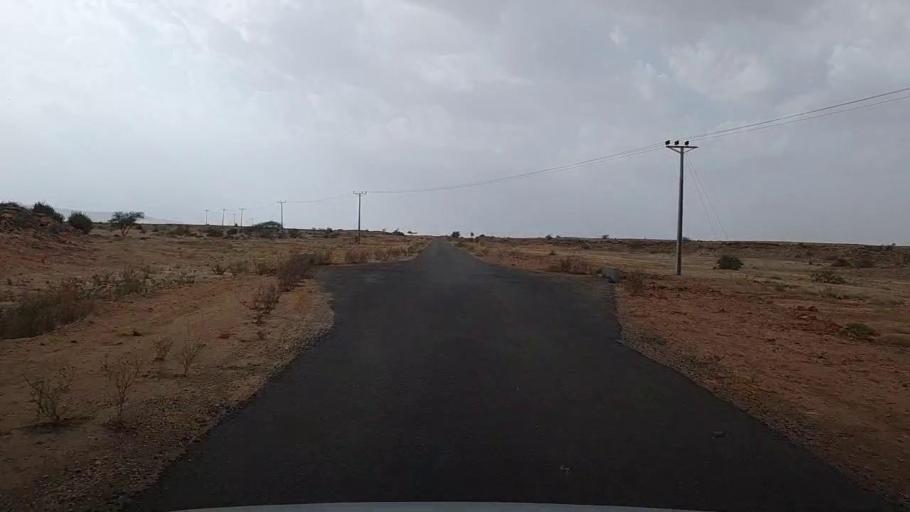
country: PK
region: Sindh
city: Jamshoro
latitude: 25.4299
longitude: 67.6881
